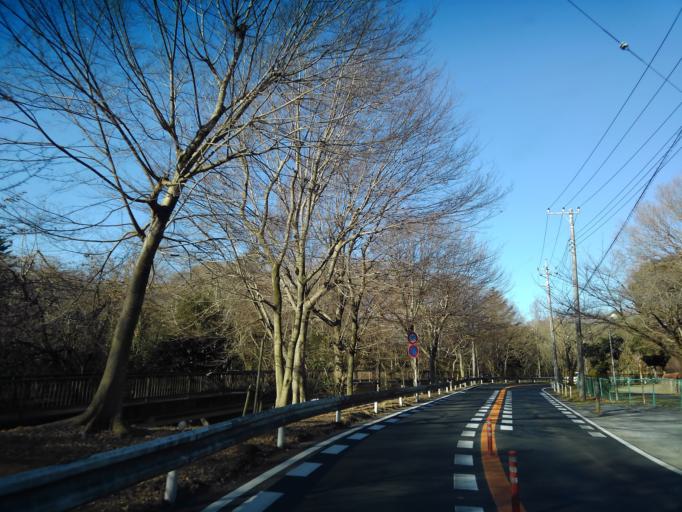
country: JP
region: Tokyo
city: Higashimurayama-shi
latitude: 35.7673
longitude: 139.4144
